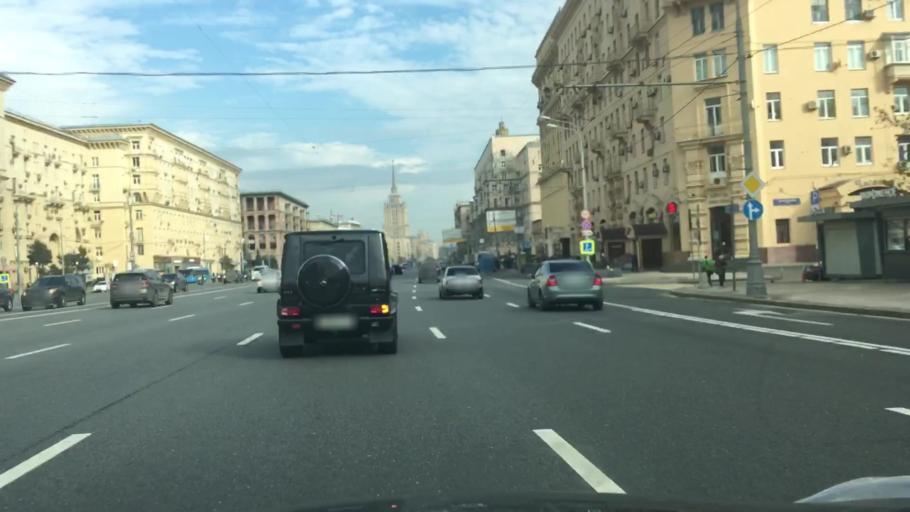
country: RU
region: Moskovskaya
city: Presnenskiy
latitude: 55.7433
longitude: 37.5442
